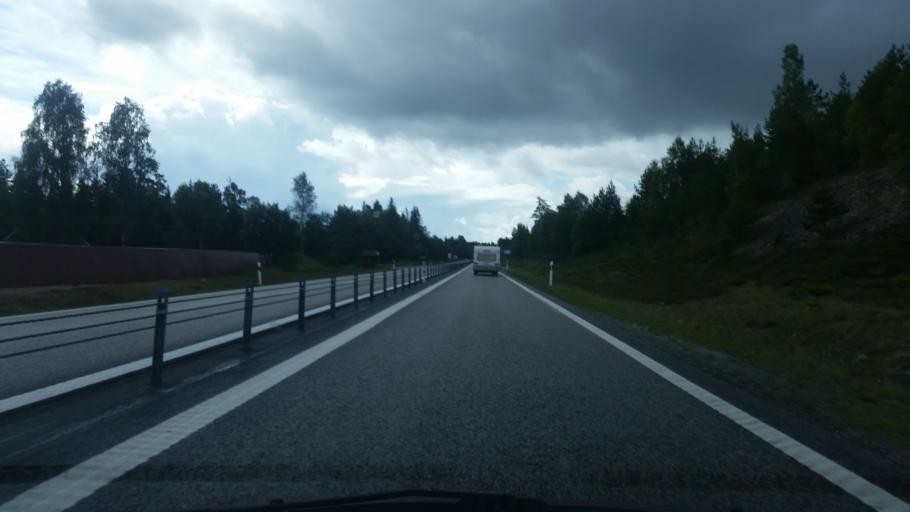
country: SE
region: Joenkoeping
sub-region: Gislaveds Kommun
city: Gislaved
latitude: 57.3368
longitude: 13.5490
